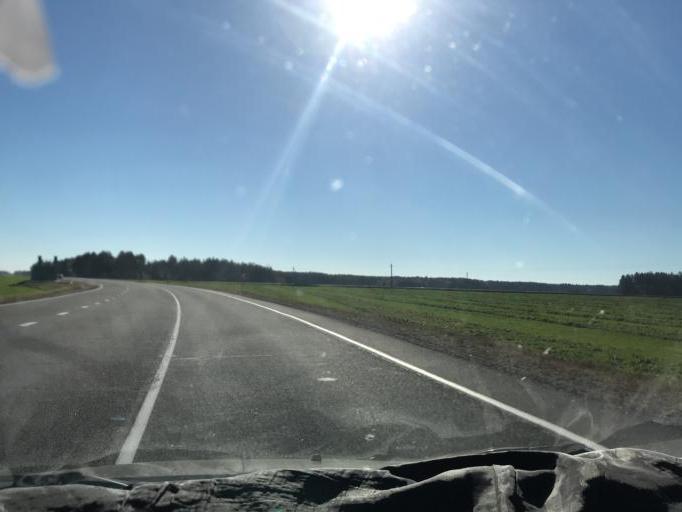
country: BY
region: Gomel
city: Parychy
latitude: 52.8726
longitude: 29.3172
